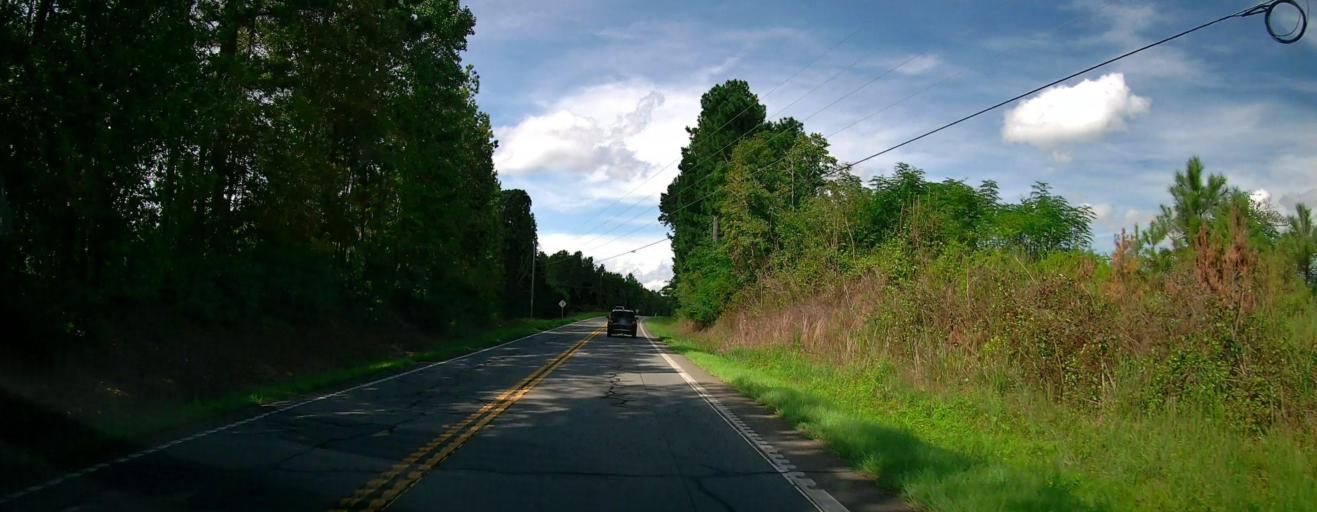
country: US
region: Georgia
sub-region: Talbot County
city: Sardis
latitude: 32.7716
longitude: -84.5578
